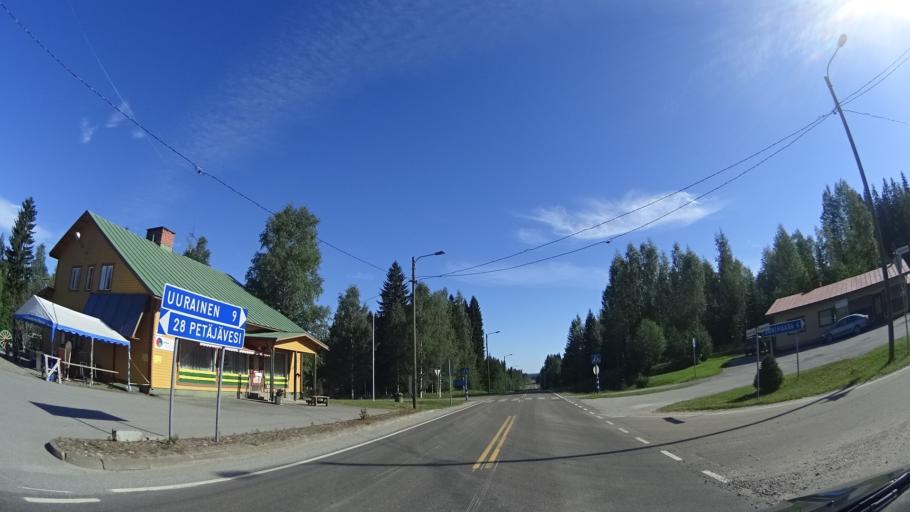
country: FI
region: Central Finland
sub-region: Jyvaeskylae
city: Uurainen
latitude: 62.4255
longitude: 25.3740
